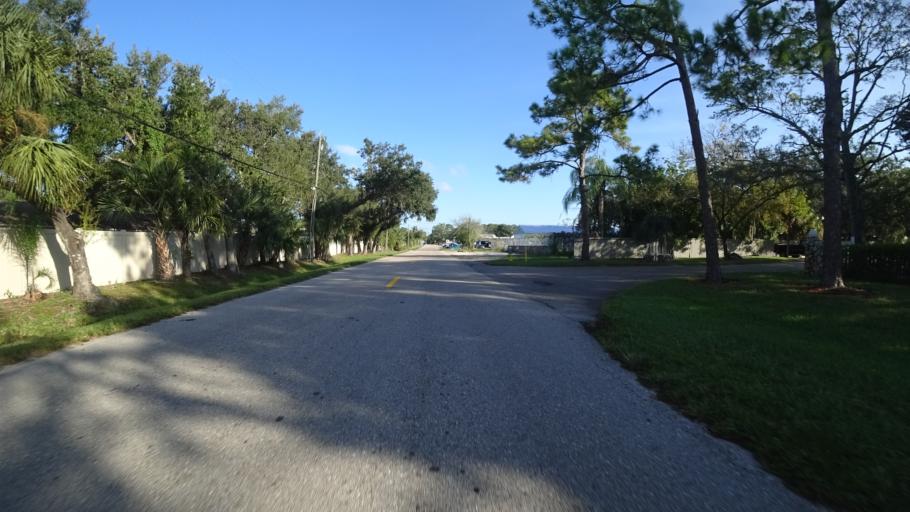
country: US
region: Florida
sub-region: Manatee County
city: West Samoset
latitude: 27.4705
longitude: -82.5650
